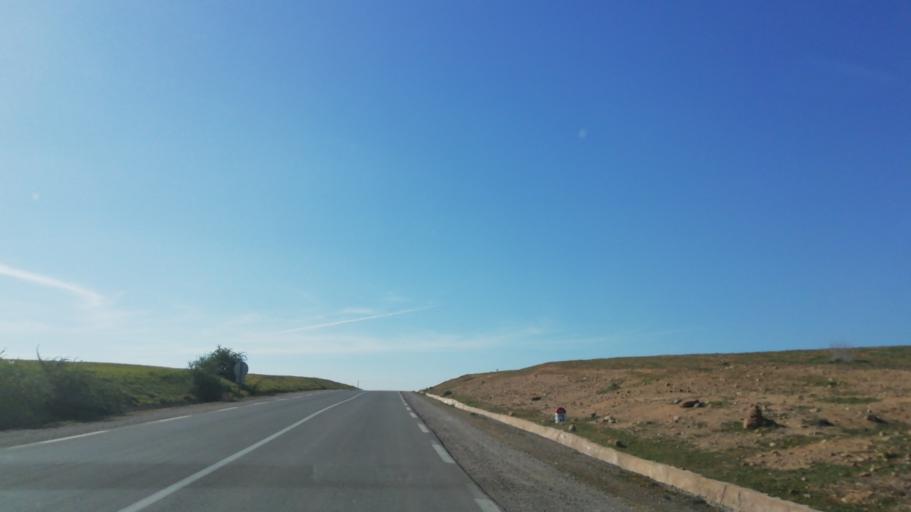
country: DZ
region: Mascara
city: Oued el Abtal
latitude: 35.4540
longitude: 0.7714
